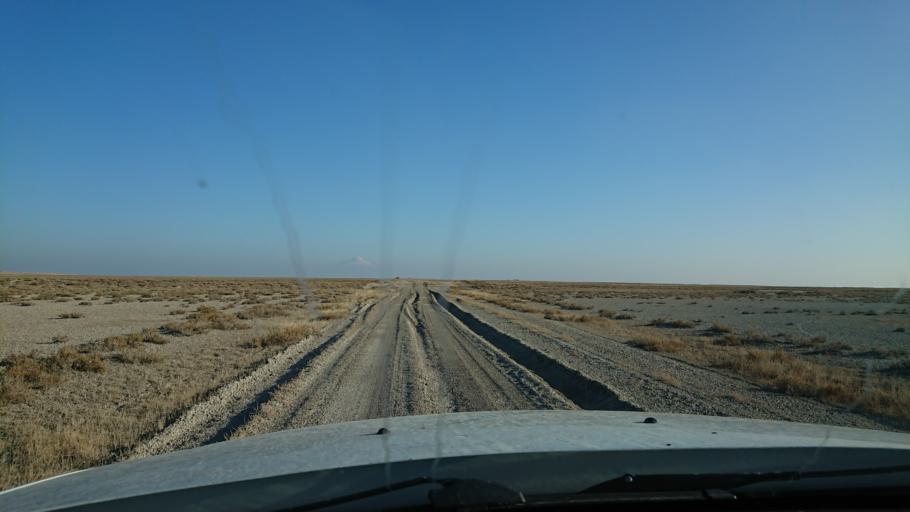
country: TR
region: Aksaray
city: Sultanhani
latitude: 38.4022
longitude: 33.5784
